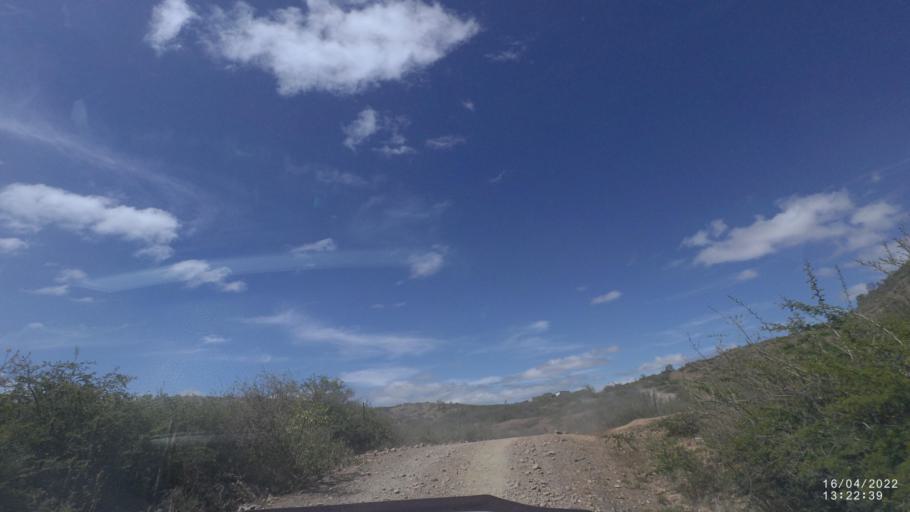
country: BO
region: Cochabamba
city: Mizque
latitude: -17.9931
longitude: -65.6049
